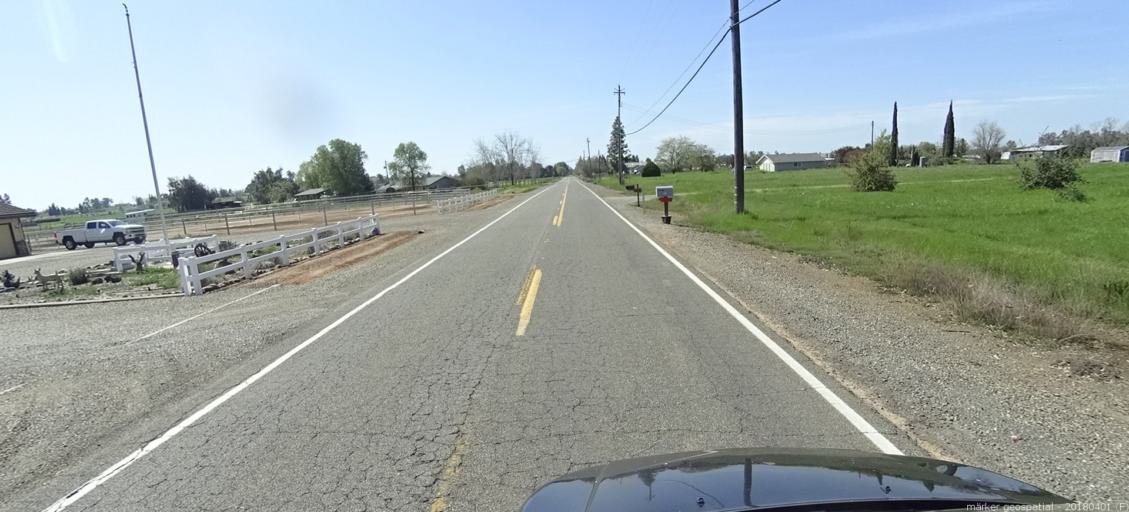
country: US
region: California
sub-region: Sacramento County
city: Wilton
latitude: 38.4086
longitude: -121.2265
